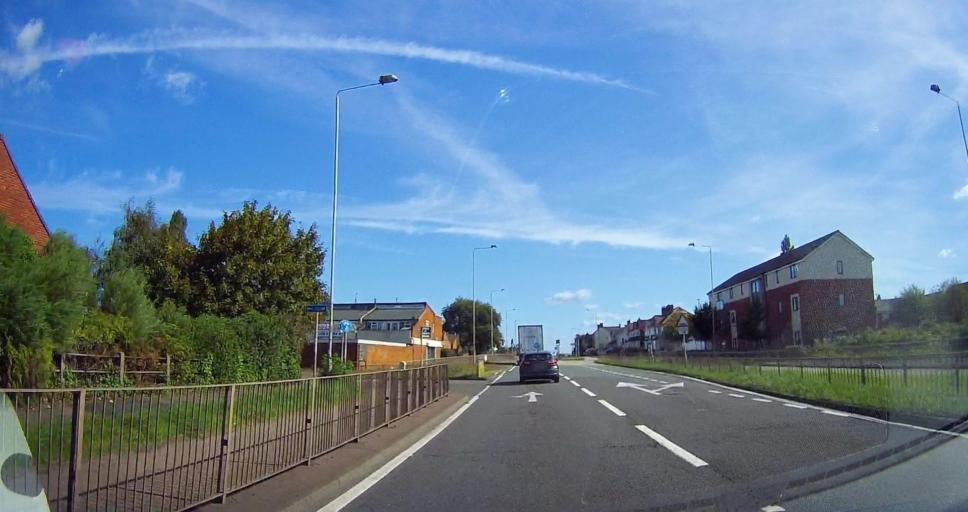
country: GB
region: England
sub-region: Staffordshire
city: Chasetown
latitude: 52.6561
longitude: -1.9326
